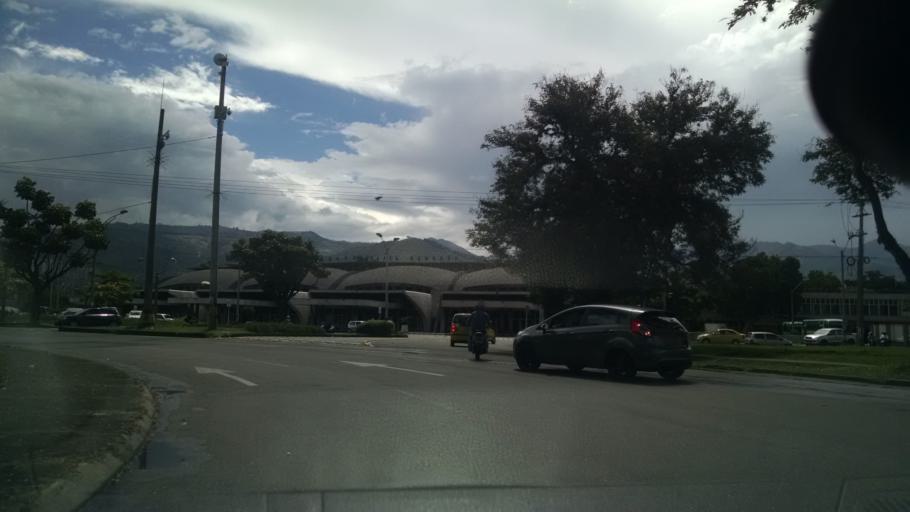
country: CO
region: Antioquia
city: Itagui
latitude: 6.2190
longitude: -75.5856
